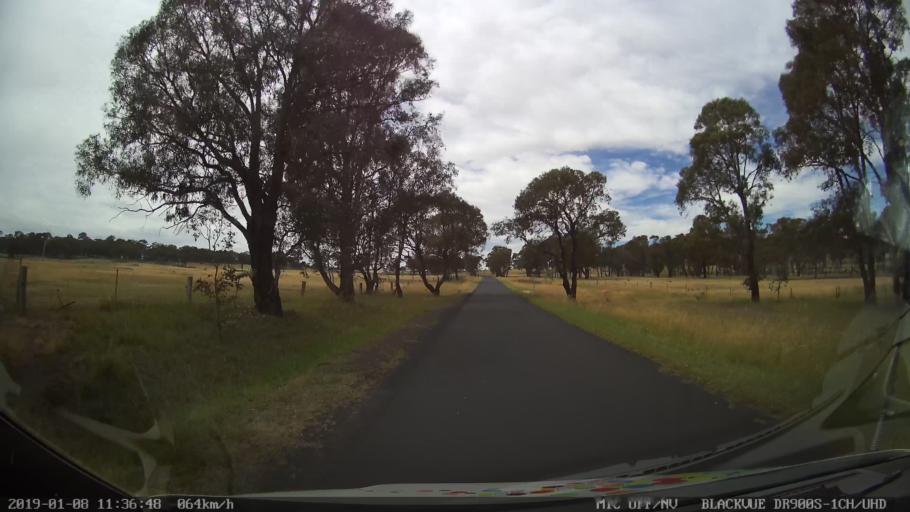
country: AU
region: New South Wales
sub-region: Guyra
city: Guyra
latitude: -30.3477
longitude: 151.5470
